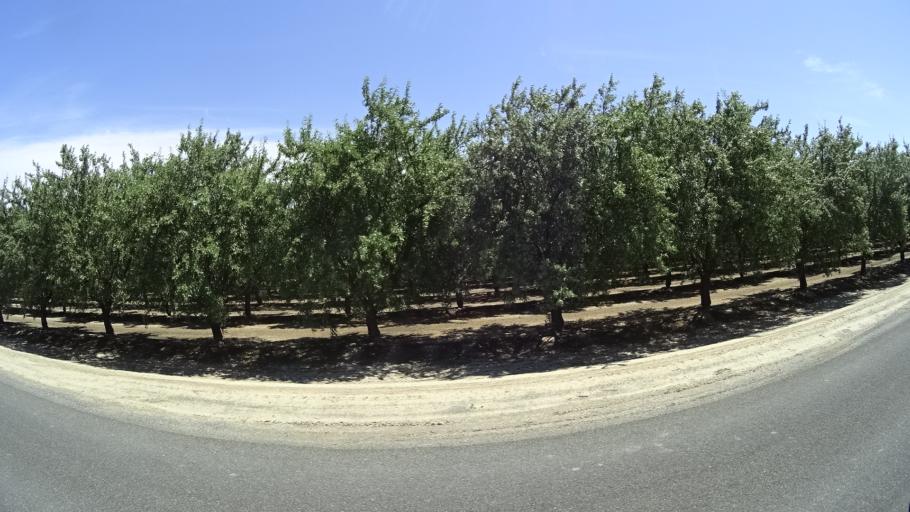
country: US
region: California
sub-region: Kings County
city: Armona
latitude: 36.3296
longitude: -119.7180
